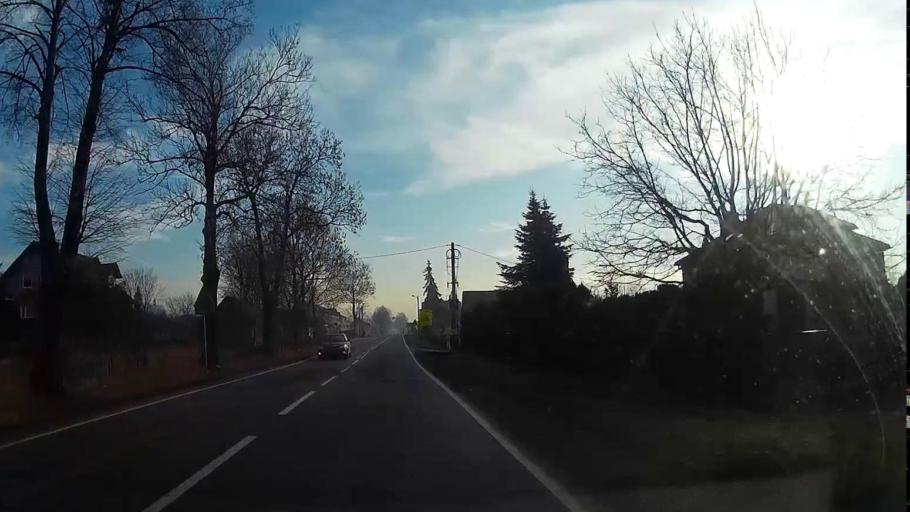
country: PL
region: Lesser Poland Voivodeship
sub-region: Powiat chrzanowski
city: Kwaczala
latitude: 50.0642
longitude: 19.4900
